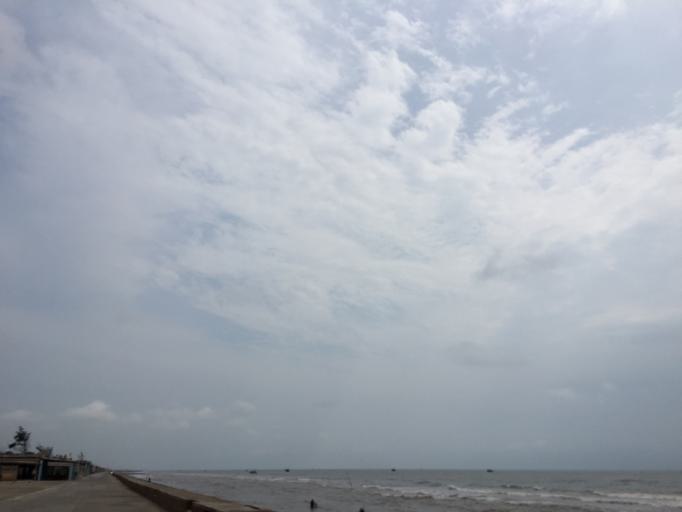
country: VN
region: Ninh Binh
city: Thi Tran Phat Diem
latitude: 20.0293
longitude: 106.2232
